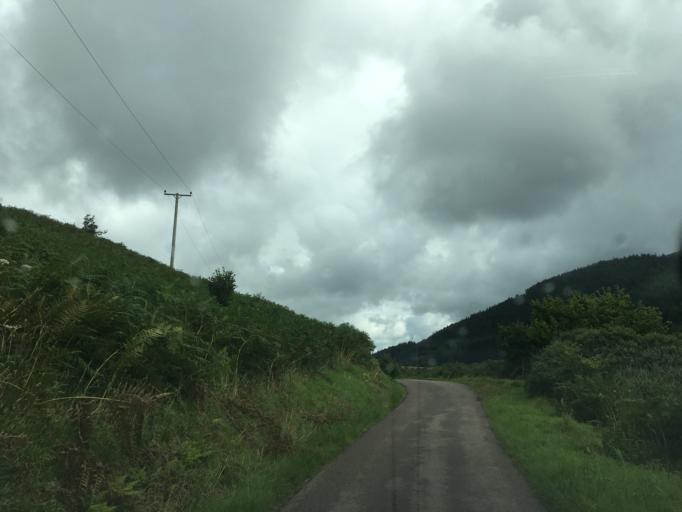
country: GB
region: Scotland
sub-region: Argyll and Bute
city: Oban
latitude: 56.2622
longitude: -5.3888
